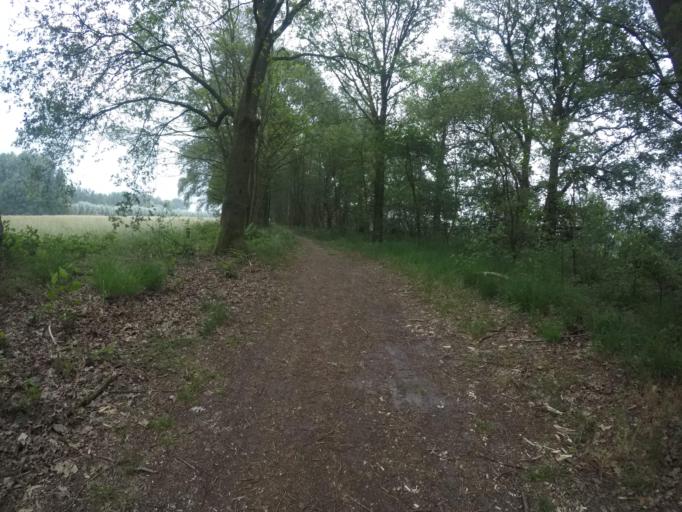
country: NL
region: Gelderland
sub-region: Gemeente Winterswijk
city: Winterswijk
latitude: 52.0402
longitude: 6.7127
